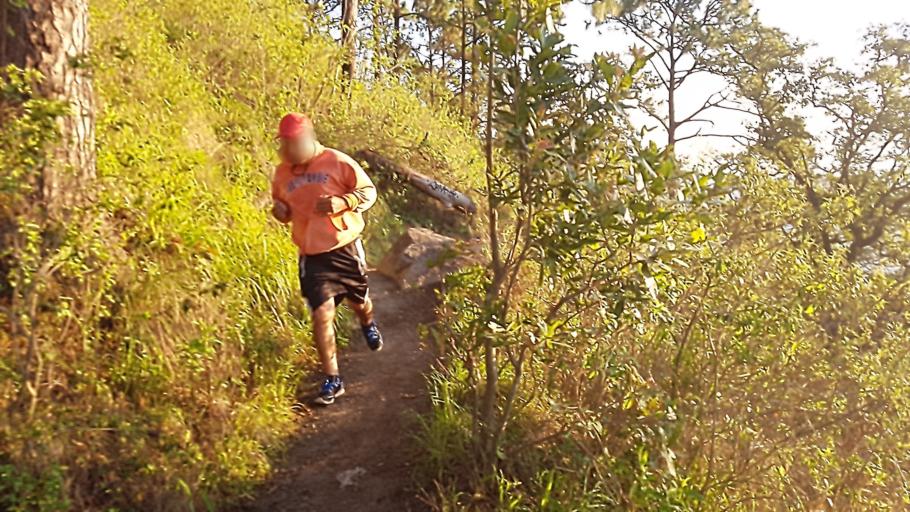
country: MX
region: Nayarit
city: Tepic
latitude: 21.5038
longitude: -104.9301
